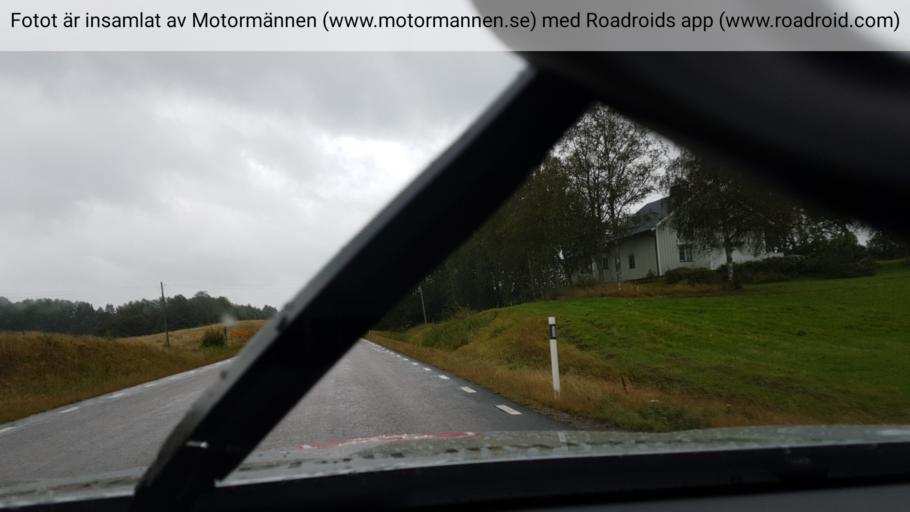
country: SE
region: Vaestra Goetaland
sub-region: Dals-Ed Kommun
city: Ed
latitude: 58.8781
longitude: 11.8881
